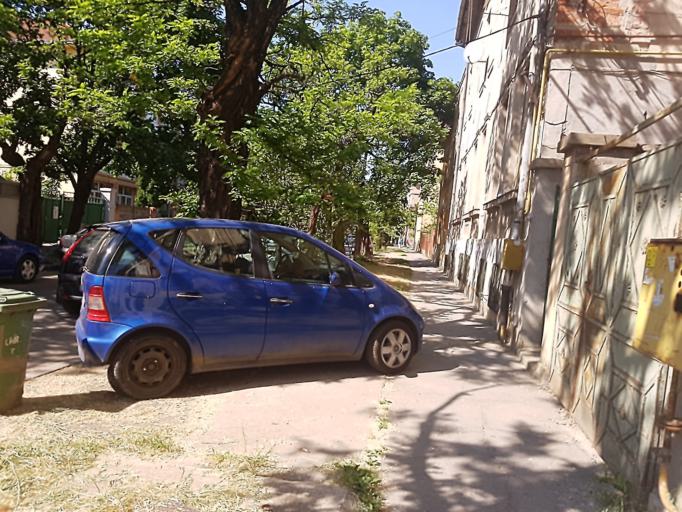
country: RO
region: Timis
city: Timisoara
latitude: 45.7409
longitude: 21.2275
